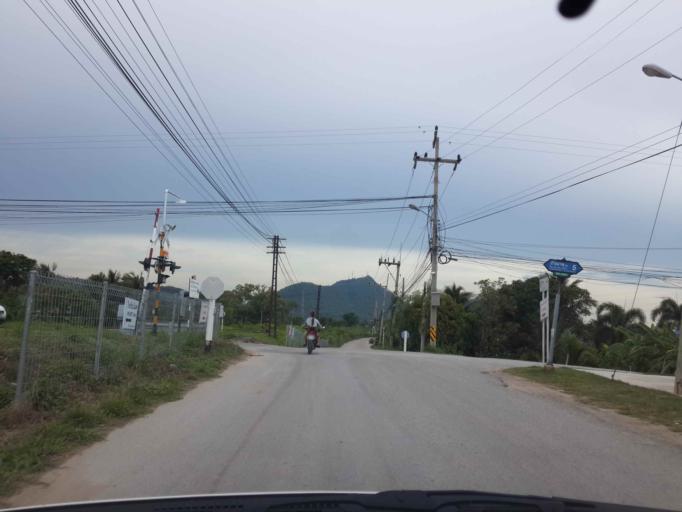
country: TH
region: Chon Buri
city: Si Racha
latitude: 13.2235
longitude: 100.9529
